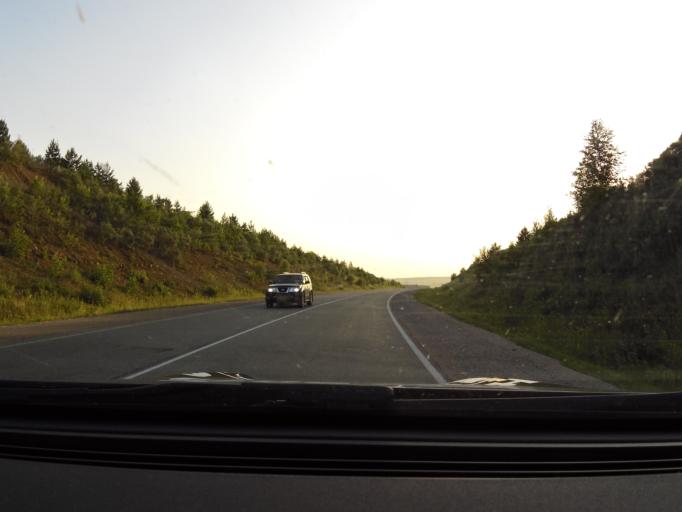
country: RU
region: Sverdlovsk
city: Mikhaylovsk
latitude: 56.4220
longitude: 59.0516
